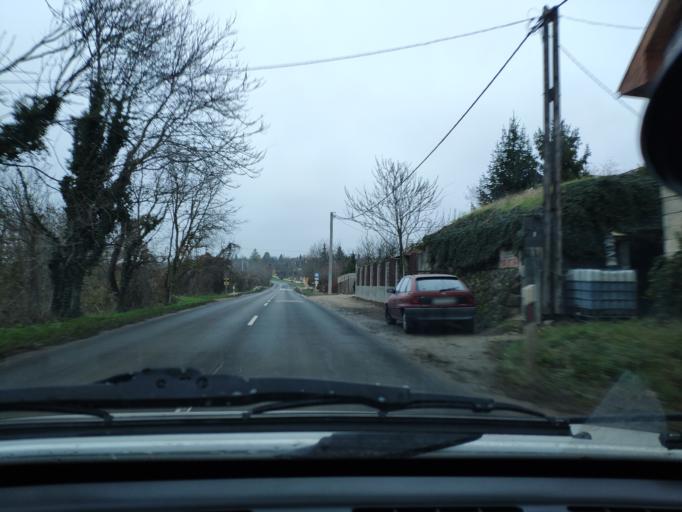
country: HU
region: Pest
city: Soskut
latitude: 47.4230
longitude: 18.8259
